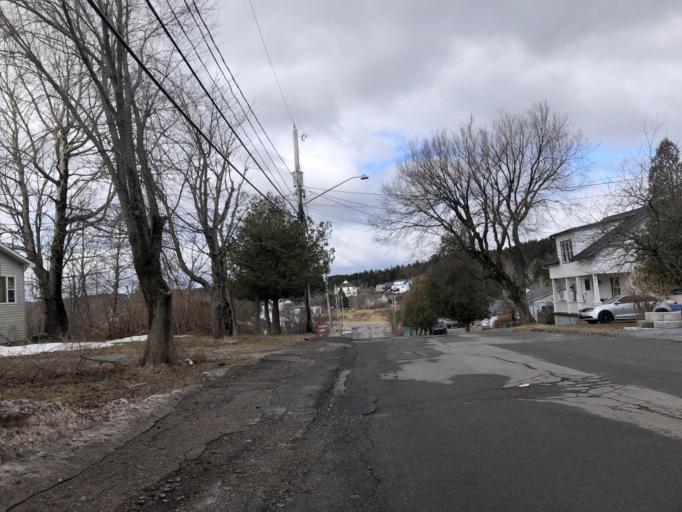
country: CA
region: New Brunswick
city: Saint John
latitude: 45.3224
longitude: -66.0119
